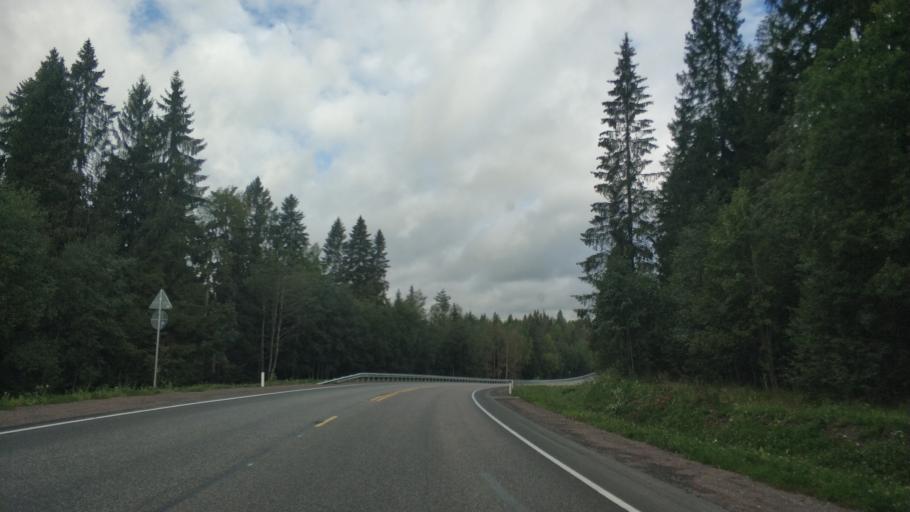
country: RU
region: Republic of Karelia
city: Khelyulya
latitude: 61.7878
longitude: 30.6346
